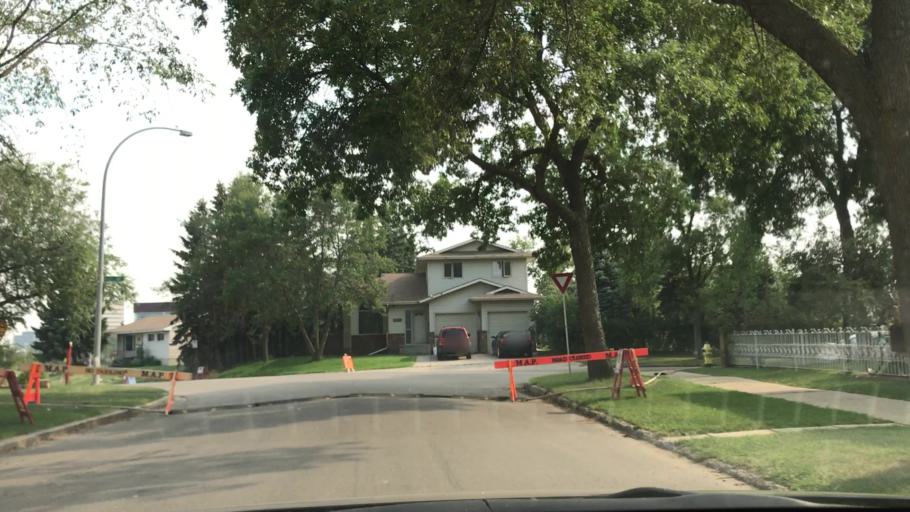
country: CA
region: Alberta
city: Edmonton
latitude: 53.5003
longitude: -113.5004
